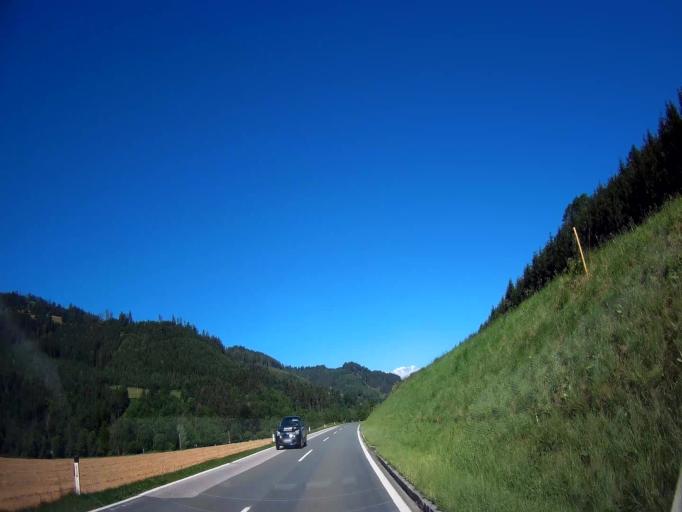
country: AT
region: Carinthia
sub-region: Politischer Bezirk Sankt Veit an der Glan
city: Bruckl
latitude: 46.7482
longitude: 14.5147
